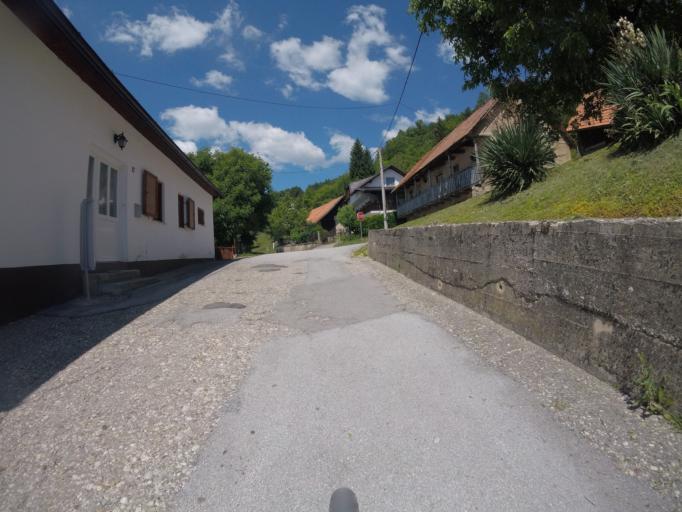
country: SI
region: Kostanjevica na Krki
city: Kostanjevica na Krki
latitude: 45.7670
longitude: 15.4550
